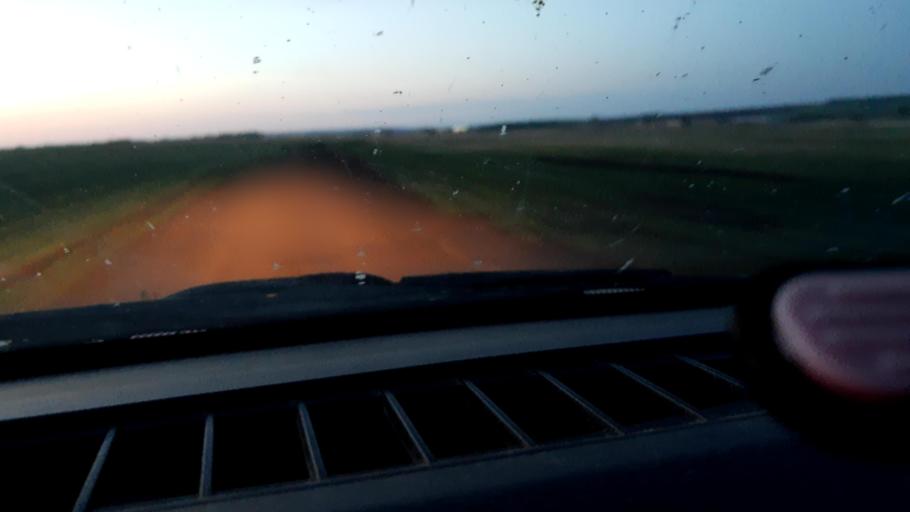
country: RU
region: Bashkortostan
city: Asanovo
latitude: 54.8592
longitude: 55.5876
